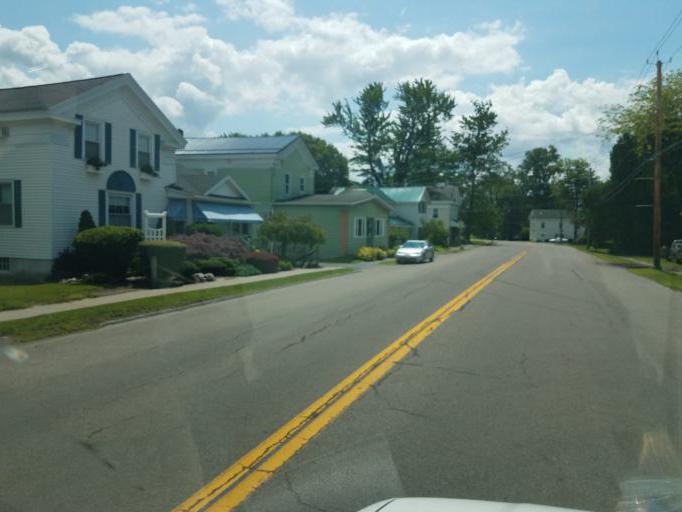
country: US
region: New York
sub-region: Wayne County
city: Clyde
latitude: 43.1528
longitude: -76.8782
